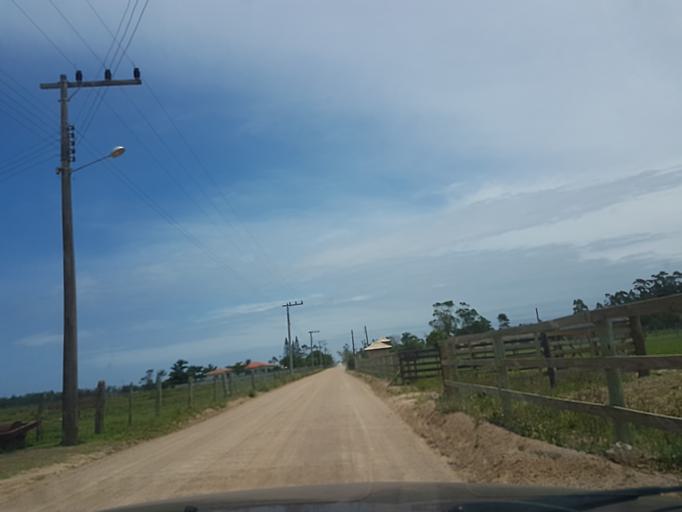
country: BR
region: Santa Catarina
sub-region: Jaguaruna
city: Jaguaruna
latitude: -28.6341
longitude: -48.9565
